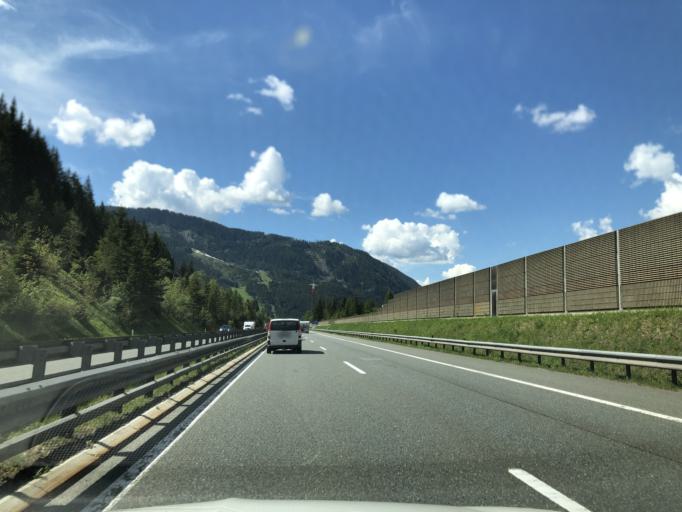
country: AT
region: Salzburg
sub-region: Politischer Bezirk Sankt Johann im Pongau
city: Flachau
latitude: 47.2842
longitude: 13.4043
